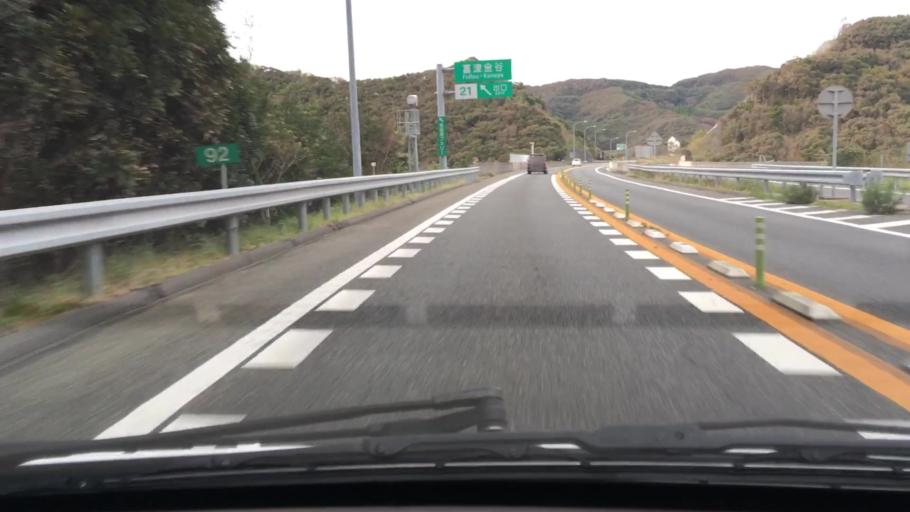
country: JP
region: Chiba
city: Futtsu
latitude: 35.1651
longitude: 139.8316
